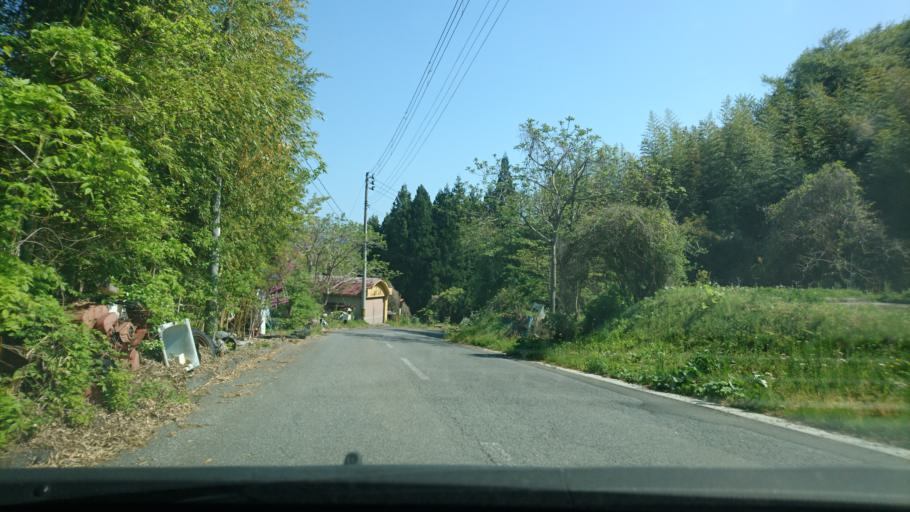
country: JP
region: Iwate
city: Ichinoseki
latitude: 38.9177
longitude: 141.2783
